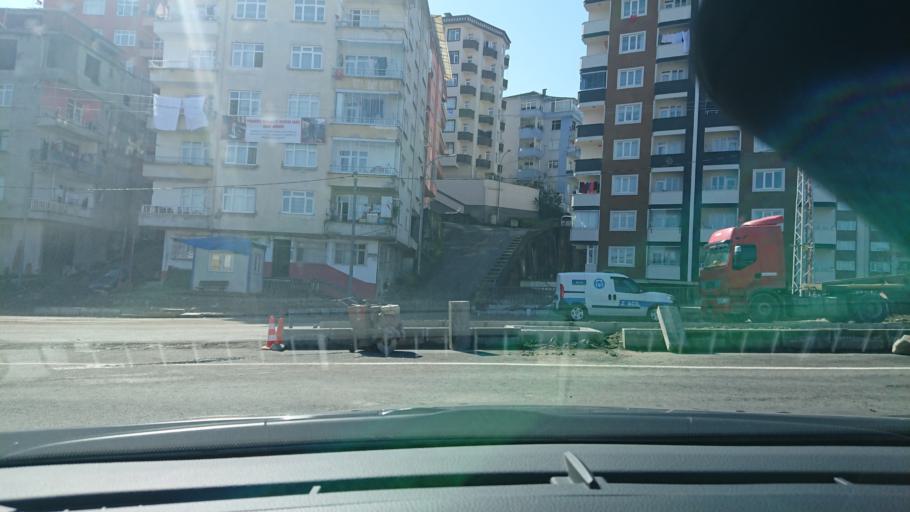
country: TR
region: Rize
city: Rize
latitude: 41.0213
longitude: 40.5281
